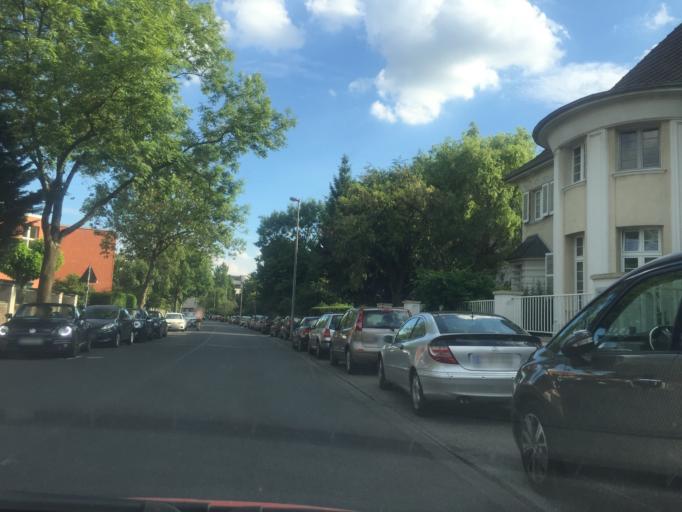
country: DE
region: North Rhine-Westphalia
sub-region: Regierungsbezirk Koln
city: Poll
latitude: 50.8946
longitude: 6.9897
